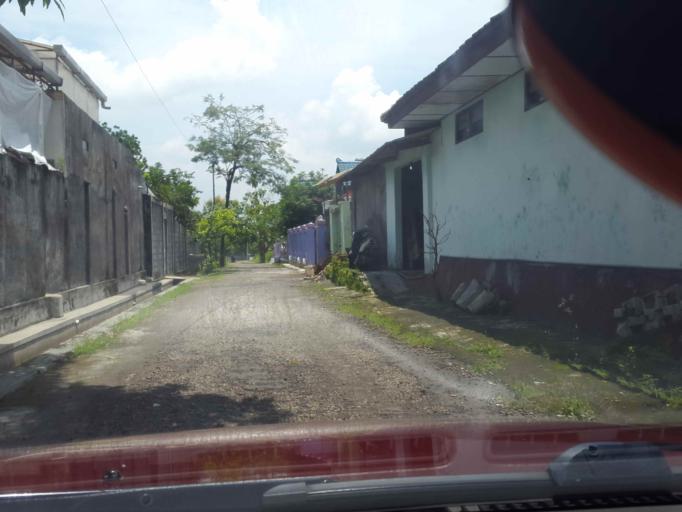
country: ID
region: Central Java
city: Jaten
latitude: -7.6041
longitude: 110.9734
